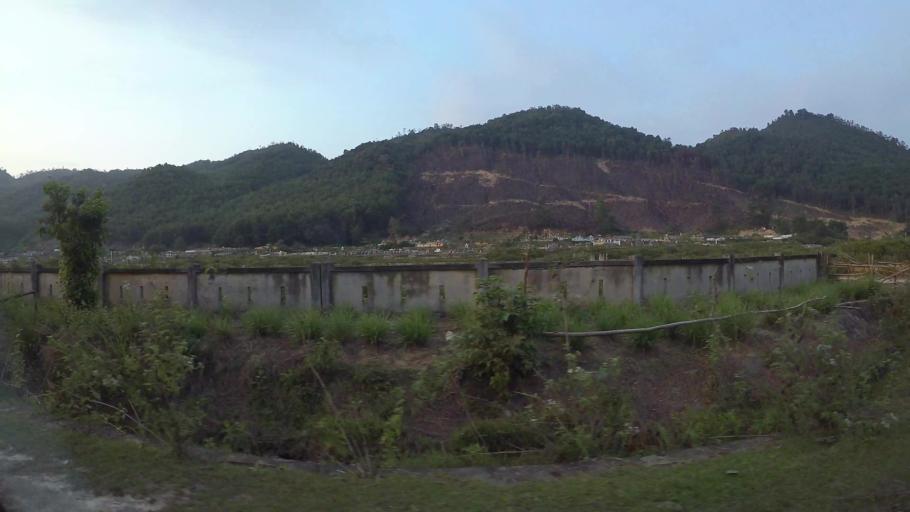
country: VN
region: Da Nang
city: Lien Chieu
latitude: 16.0596
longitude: 108.1262
